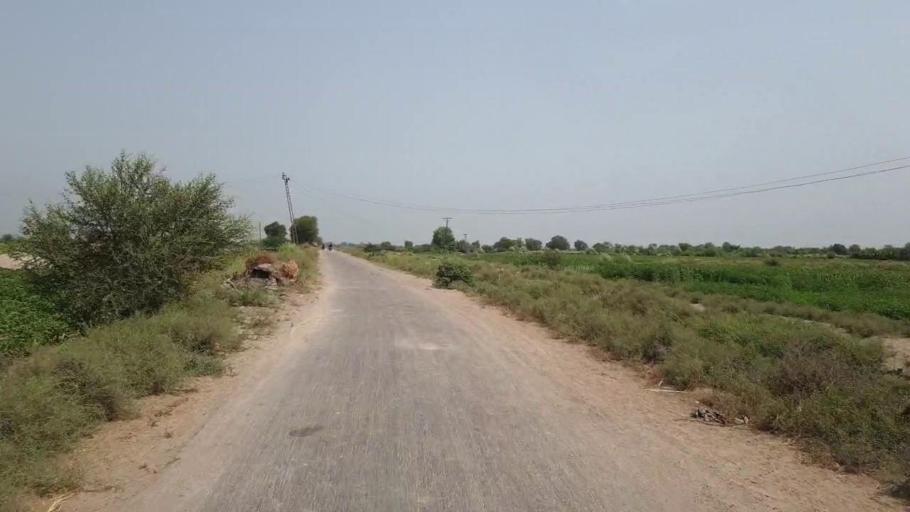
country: PK
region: Sindh
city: Nawabshah
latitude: 26.2672
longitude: 68.3167
